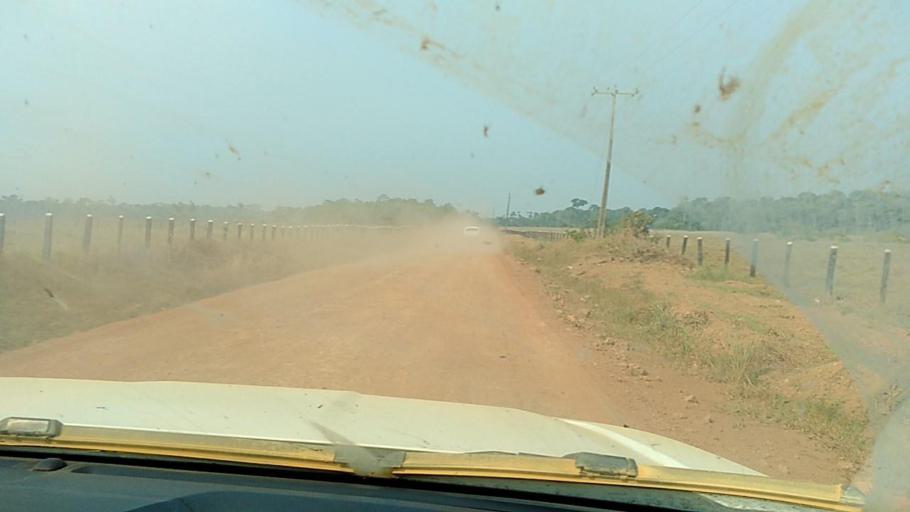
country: BR
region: Rondonia
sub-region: Porto Velho
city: Porto Velho
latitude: -8.7806
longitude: -64.0871
